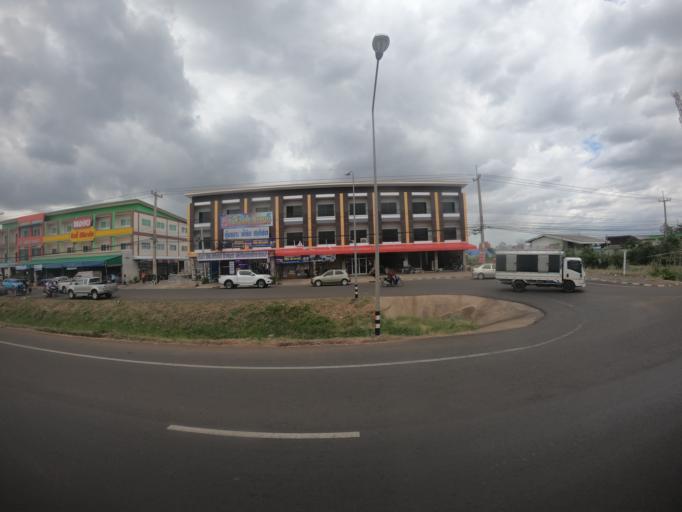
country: TH
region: Buriram
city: Nong Ki
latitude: 14.6817
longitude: 102.5486
